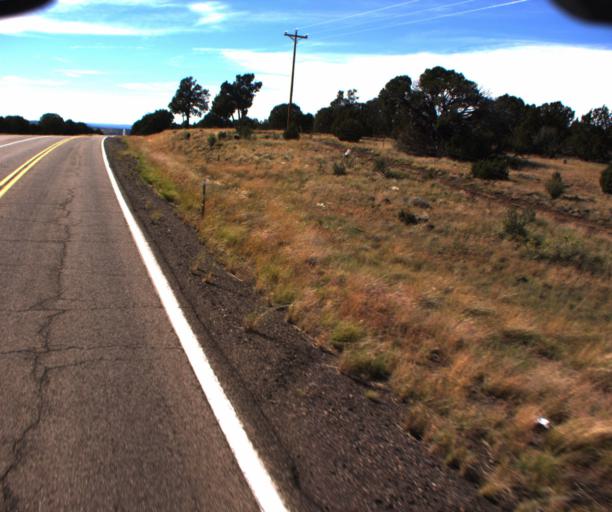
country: US
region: Arizona
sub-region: Navajo County
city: White Mountain Lake
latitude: 34.2907
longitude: -109.8102
